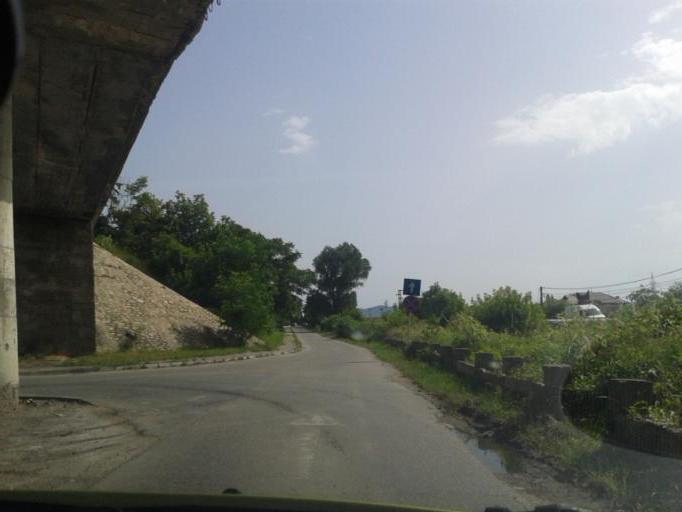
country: RO
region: Valcea
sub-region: Oras Ocnele Mari
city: Ocnele Mari
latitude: 45.0720
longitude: 24.3452
